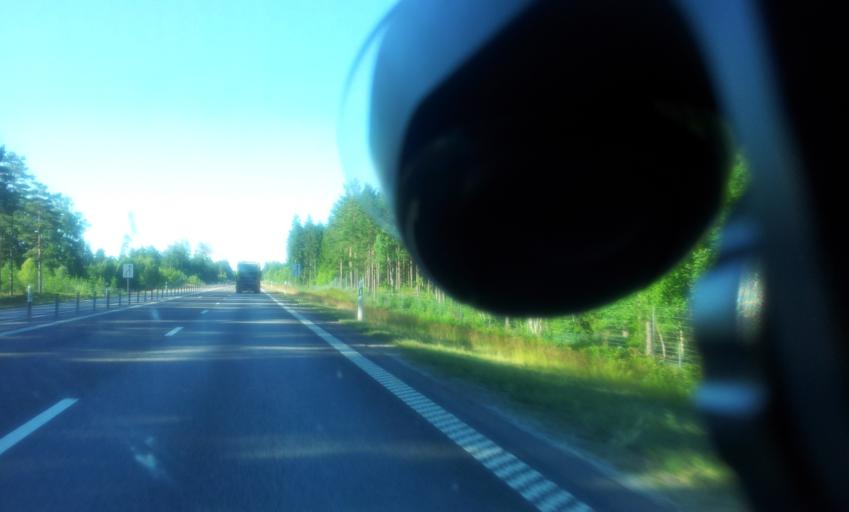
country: SE
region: Kalmar
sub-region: Kalmar Kommun
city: Ljungbyholm
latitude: 56.5309
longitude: 16.0840
